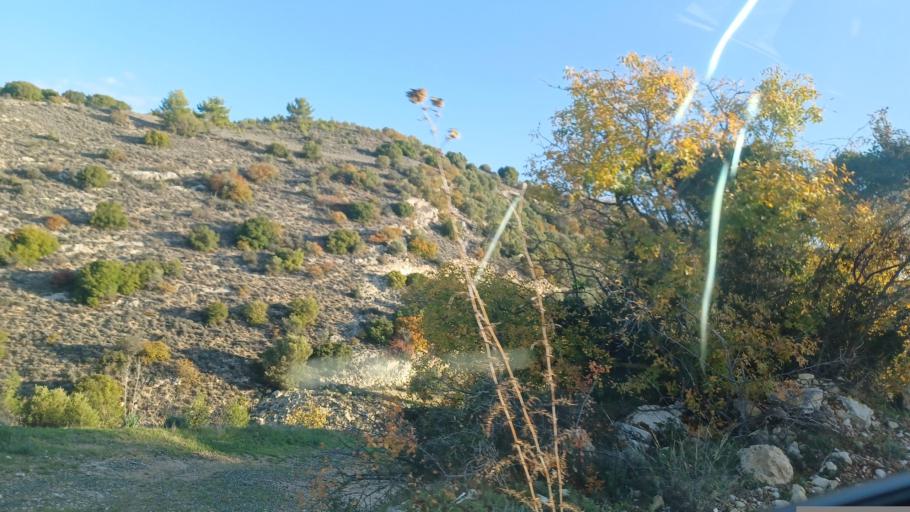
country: CY
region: Pafos
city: Mesogi
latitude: 34.8687
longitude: 32.5750
